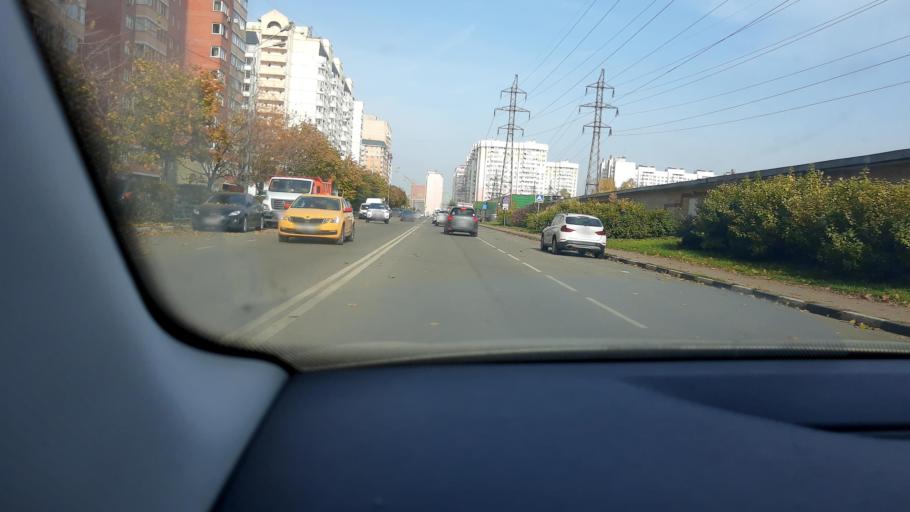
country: RU
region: Moskovskaya
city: Kotel'niki
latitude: 55.6624
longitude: 37.8586
